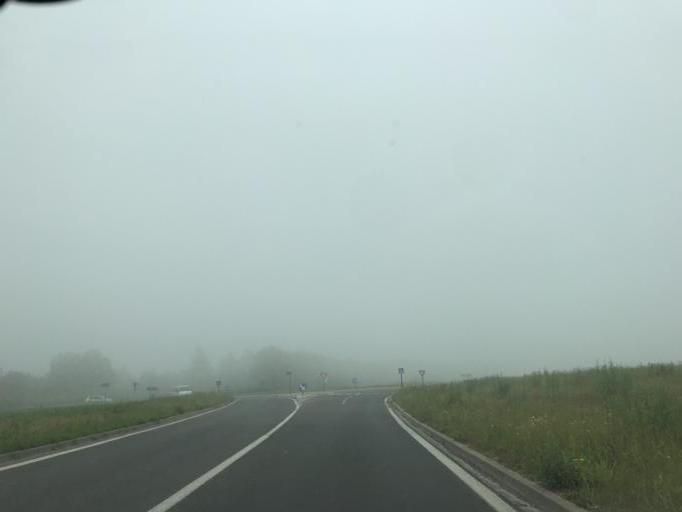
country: FR
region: Ile-de-France
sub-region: Departement de Seine-et-Marne
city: Coupvray
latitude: 48.8785
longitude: 2.8056
